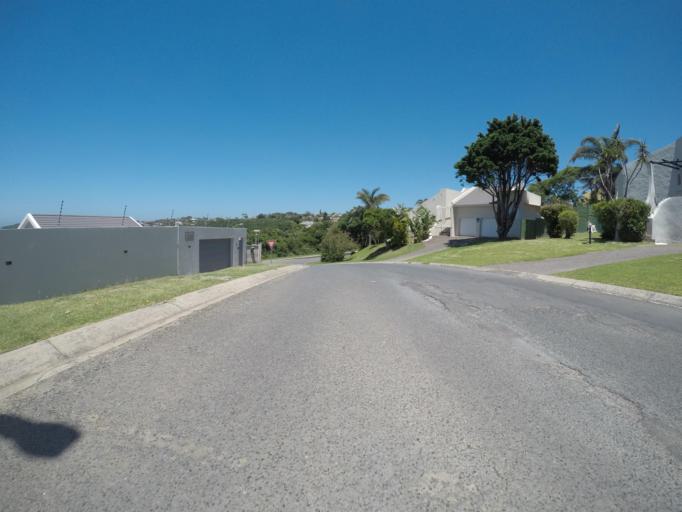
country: ZA
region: Eastern Cape
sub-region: Buffalo City Metropolitan Municipality
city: East London
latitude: -32.9620
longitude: 27.9587
